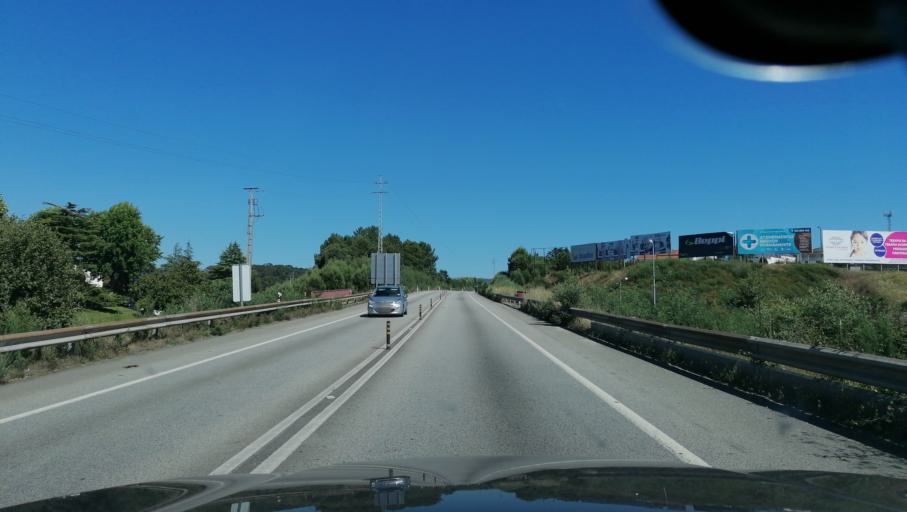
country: PT
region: Aveiro
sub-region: Santa Maria da Feira
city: Arrifana
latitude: 40.9203
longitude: -8.4981
